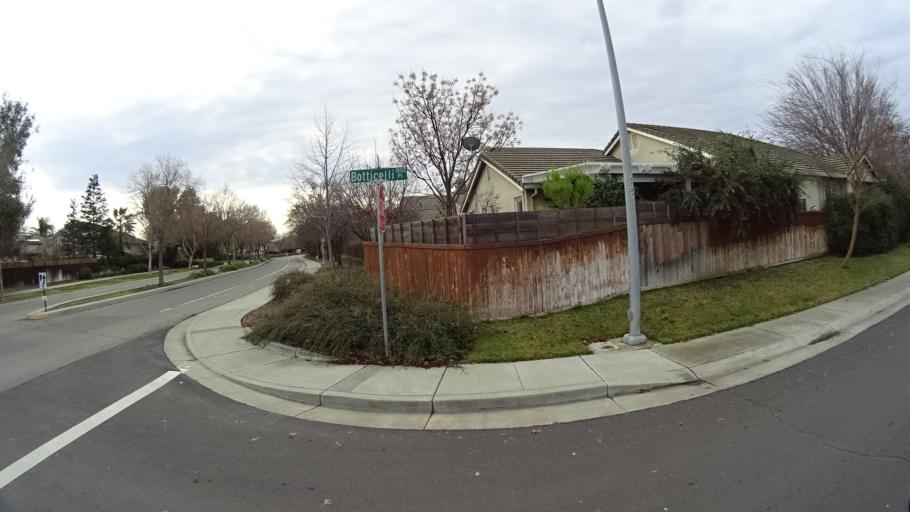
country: US
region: California
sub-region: Yolo County
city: Davis
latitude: 38.5675
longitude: -121.7261
